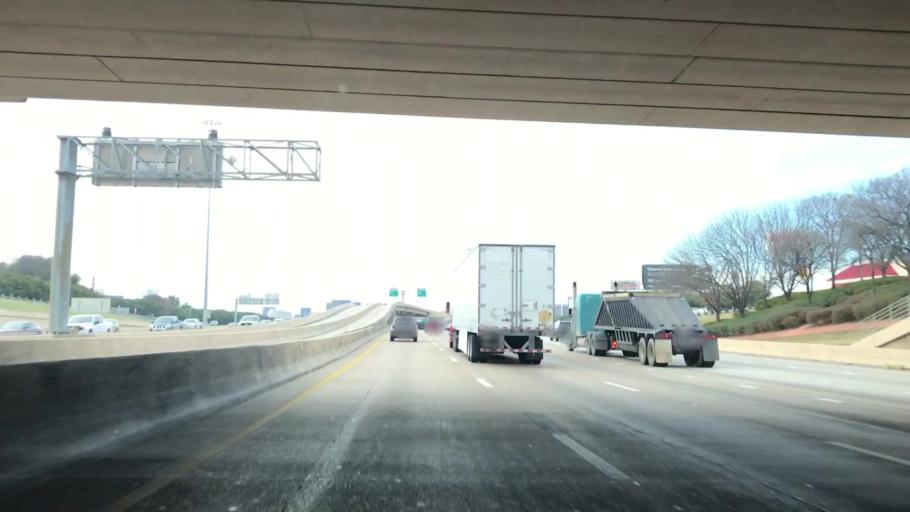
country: US
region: Texas
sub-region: Dallas County
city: Richardson
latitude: 32.9347
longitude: -96.7526
